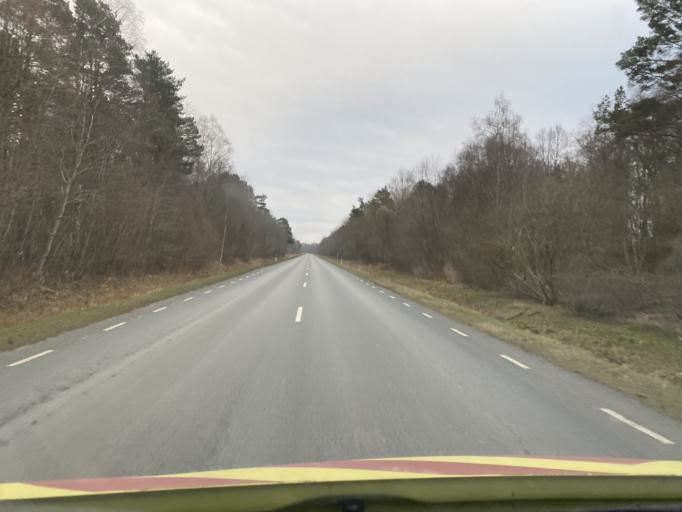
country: EE
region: Laeaene
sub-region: Ridala Parish
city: Uuemoisa
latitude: 58.8500
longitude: 23.6407
